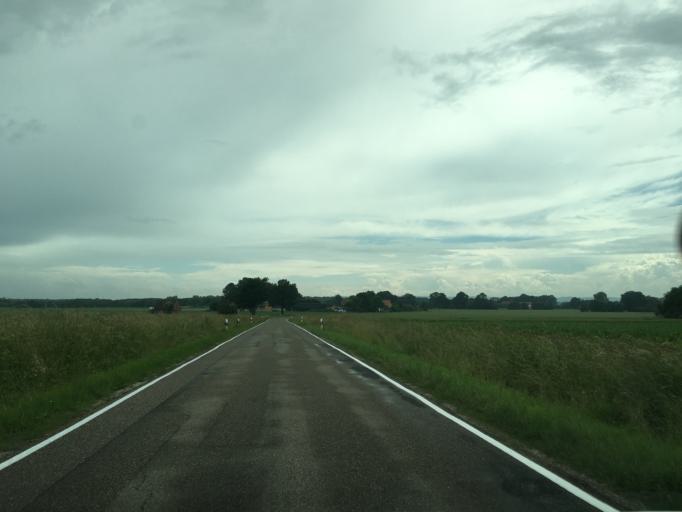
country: DE
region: North Rhine-Westphalia
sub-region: Regierungsbezirk Munster
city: Altenberge
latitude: 52.0292
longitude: 7.4641
